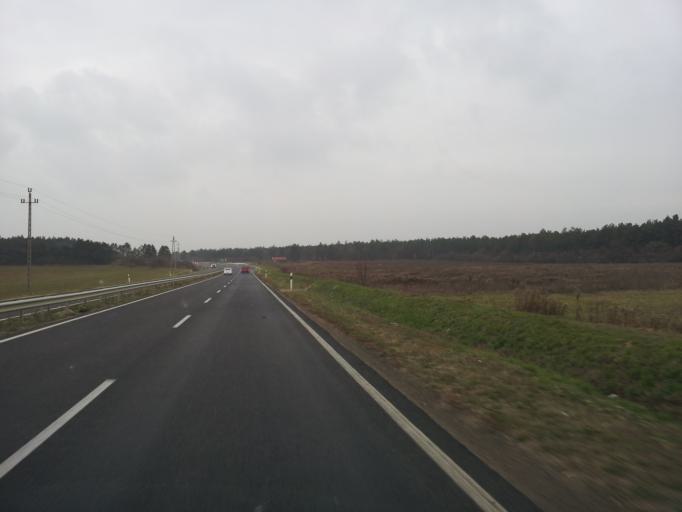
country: HU
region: Veszprem
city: Nemesvamos
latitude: 47.1168
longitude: 17.8431
